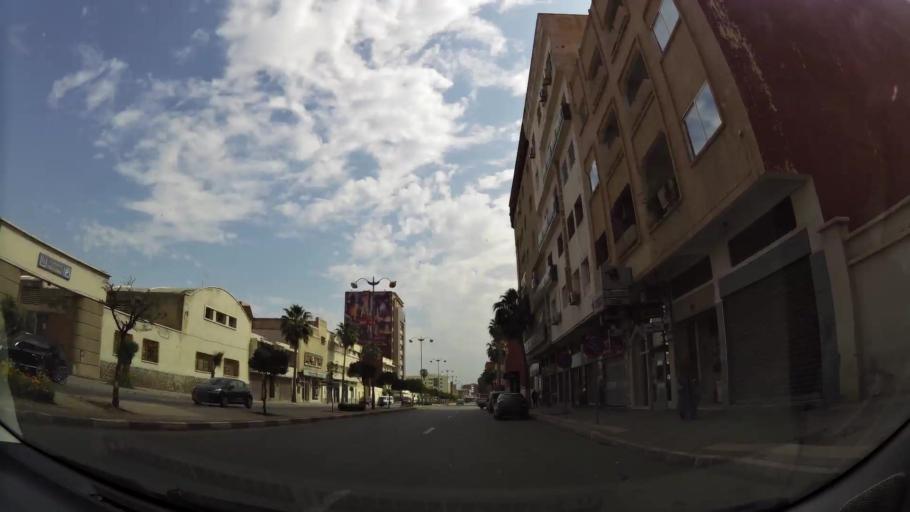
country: MA
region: Oriental
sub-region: Oujda-Angad
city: Oujda
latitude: 34.6900
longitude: -1.9090
